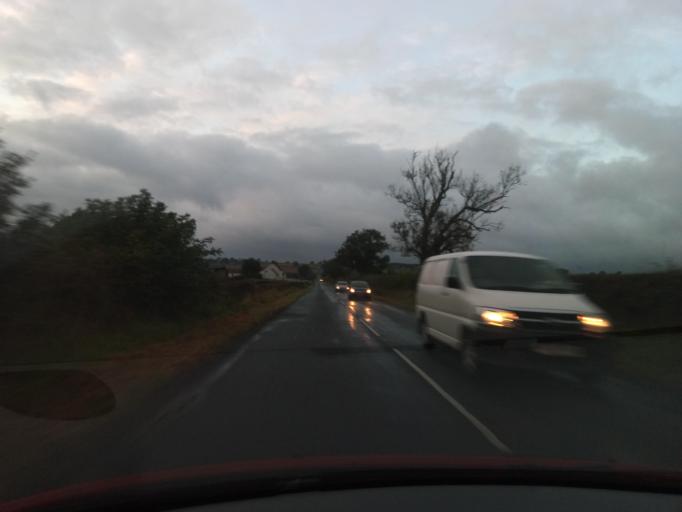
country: GB
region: England
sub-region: Darlington
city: Summerhouse
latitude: 54.5822
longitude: -1.6788
